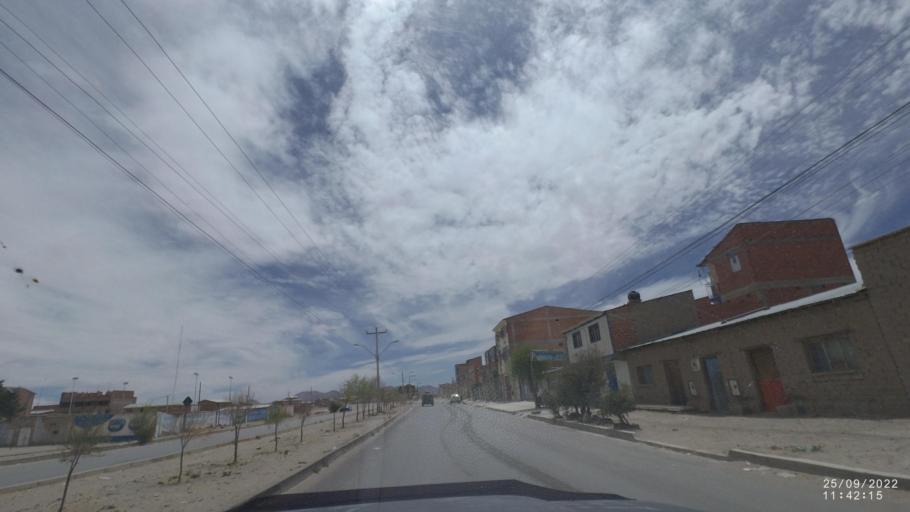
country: BO
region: Oruro
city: Challapata
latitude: -18.8986
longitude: -66.7766
